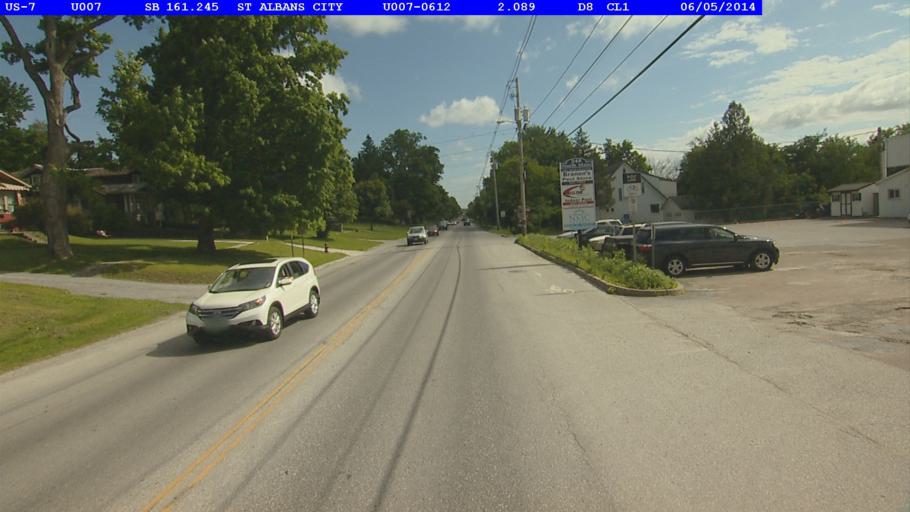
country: US
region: Vermont
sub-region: Franklin County
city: Saint Albans
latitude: 44.8228
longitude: -73.0812
